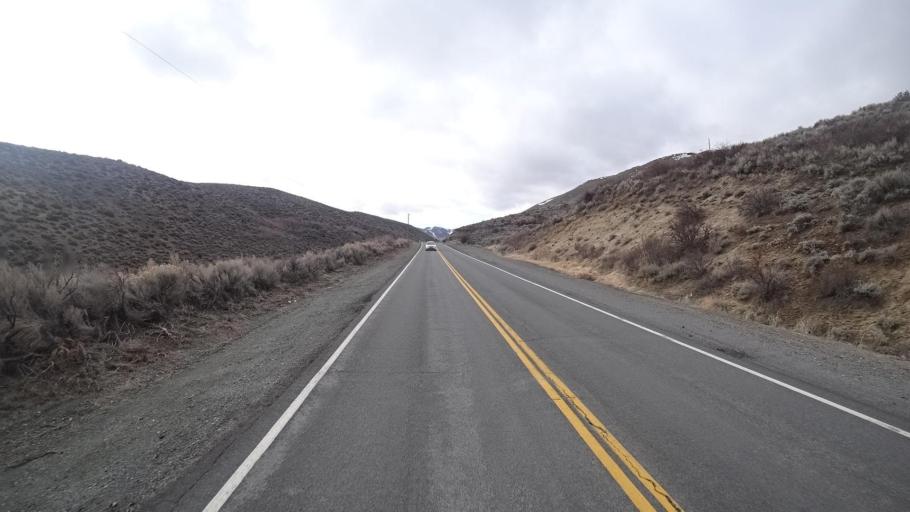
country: US
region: Nevada
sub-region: Washoe County
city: Cold Springs
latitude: 39.8287
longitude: -119.9384
